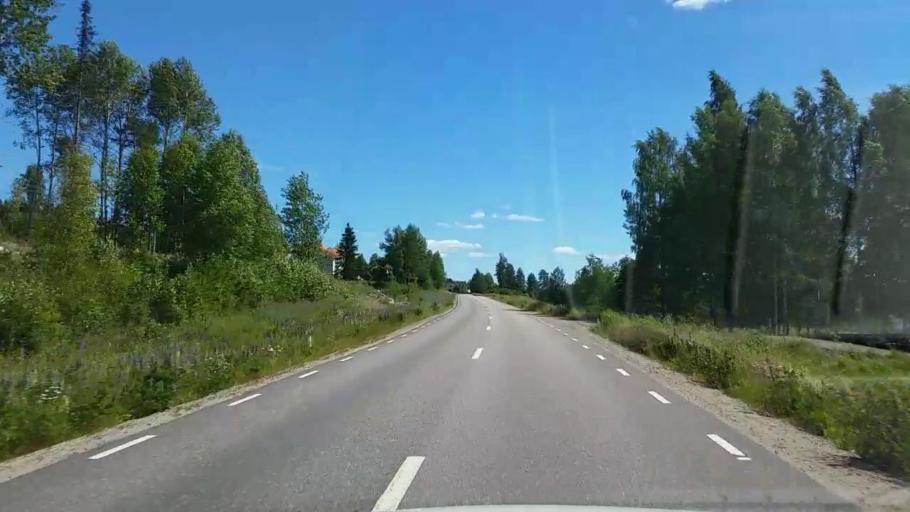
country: SE
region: Gaevleborg
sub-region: Ovanakers Kommun
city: Edsbyn
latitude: 61.4150
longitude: 15.7561
